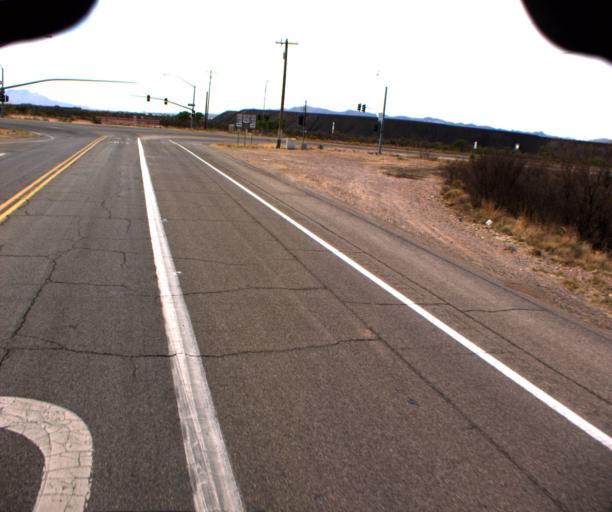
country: US
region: Arizona
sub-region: Cochise County
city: Pirtleville
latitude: 31.3533
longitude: -109.5795
